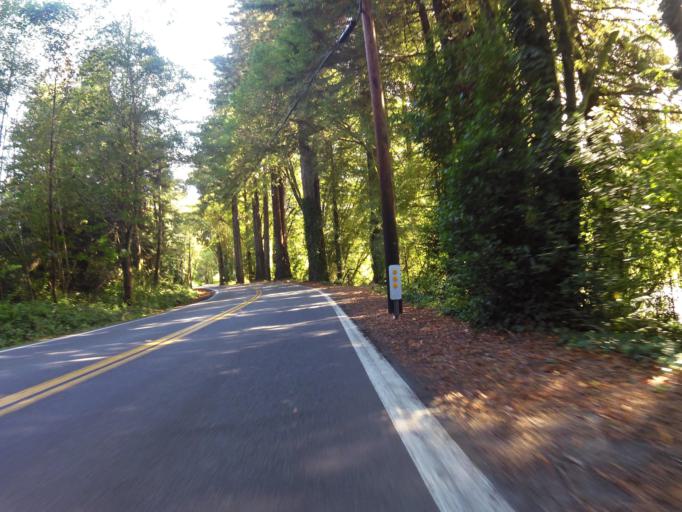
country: US
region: California
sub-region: Del Norte County
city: Bertsch-Oceanview
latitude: 41.8516
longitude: -124.1208
